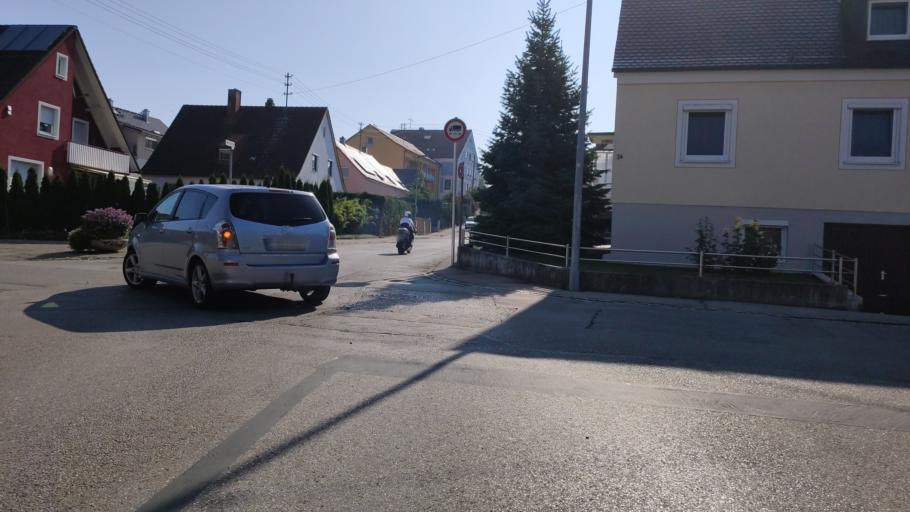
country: DE
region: Bavaria
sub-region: Swabia
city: Bobingen
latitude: 48.2724
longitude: 10.8337
